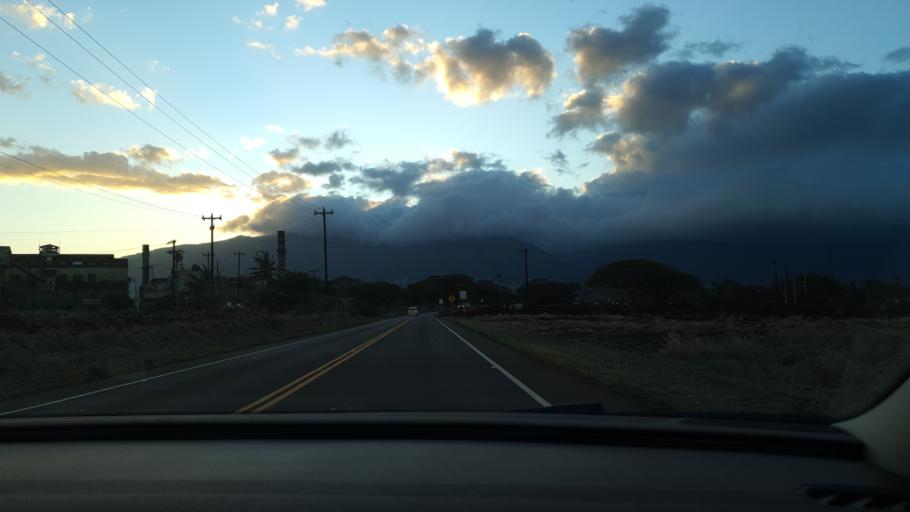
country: US
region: Hawaii
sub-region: Maui County
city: Kahului
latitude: 20.8692
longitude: -156.4499
